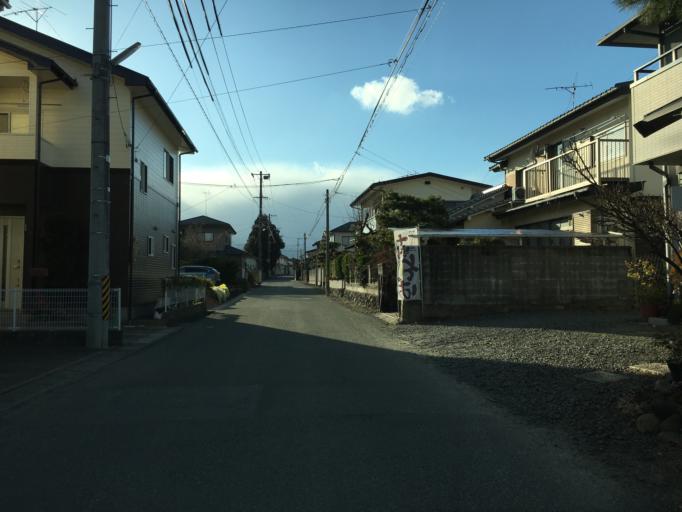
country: JP
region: Fukushima
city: Fukushima-shi
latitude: 37.7799
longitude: 140.4373
